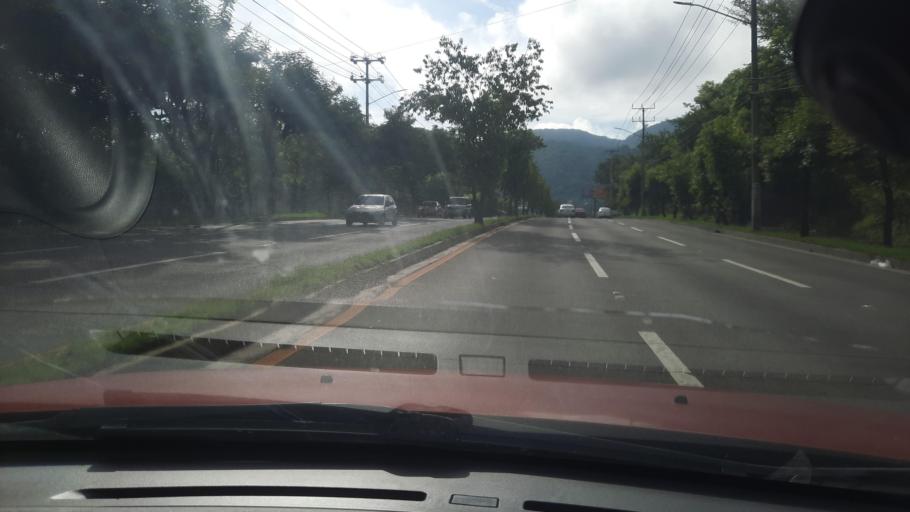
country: SV
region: San Salvador
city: San Salvador
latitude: 13.6745
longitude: -89.1999
